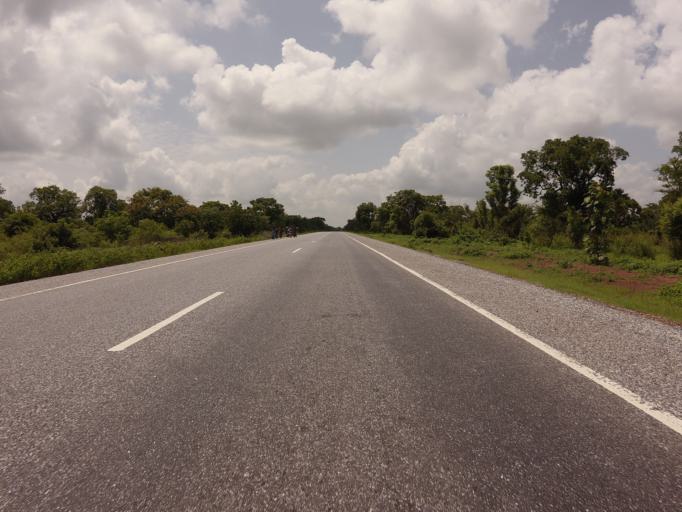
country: GH
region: Northern
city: Tamale
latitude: 9.1503
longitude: -1.3869
